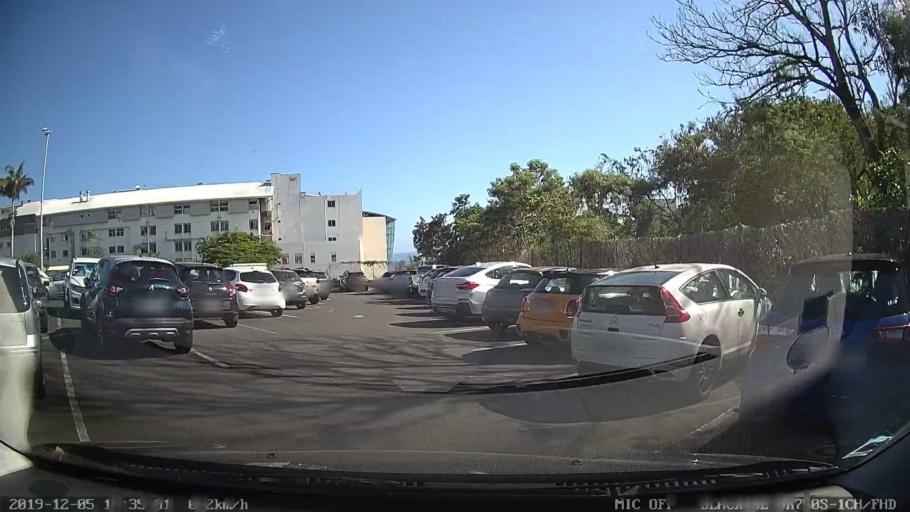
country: RE
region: Reunion
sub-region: Reunion
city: Saint-Denis
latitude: -20.9034
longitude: 55.4792
